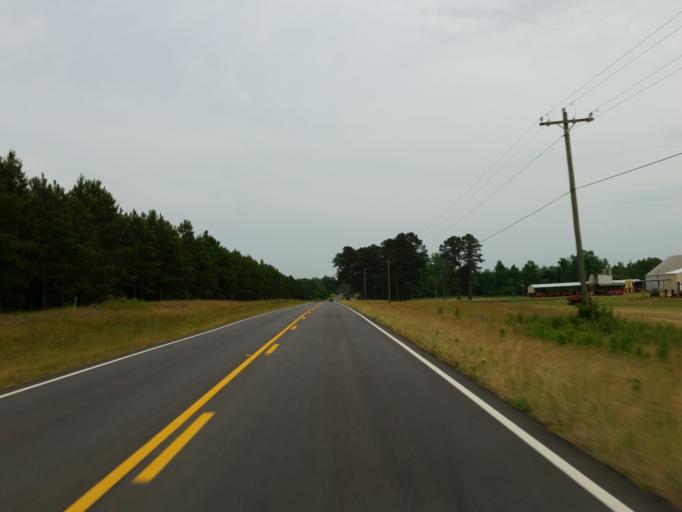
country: US
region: Georgia
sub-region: Dooly County
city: Unadilla
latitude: 32.2823
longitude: -83.7453
